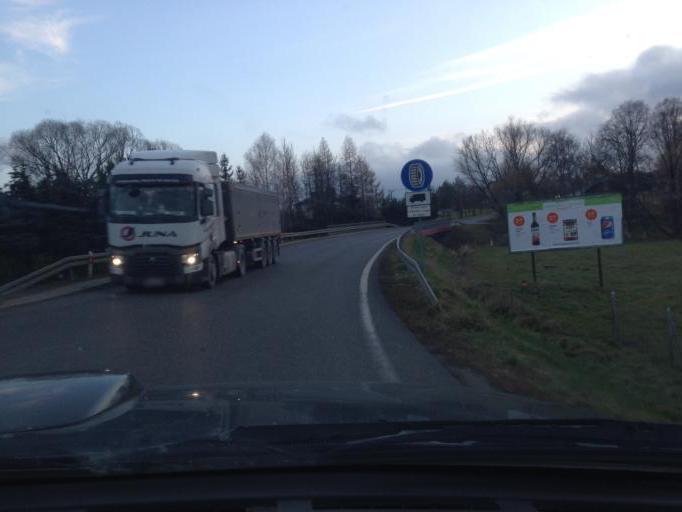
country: PL
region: Subcarpathian Voivodeship
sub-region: Powiat jasielski
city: Nowy Zmigrod
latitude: 49.6224
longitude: 21.5393
